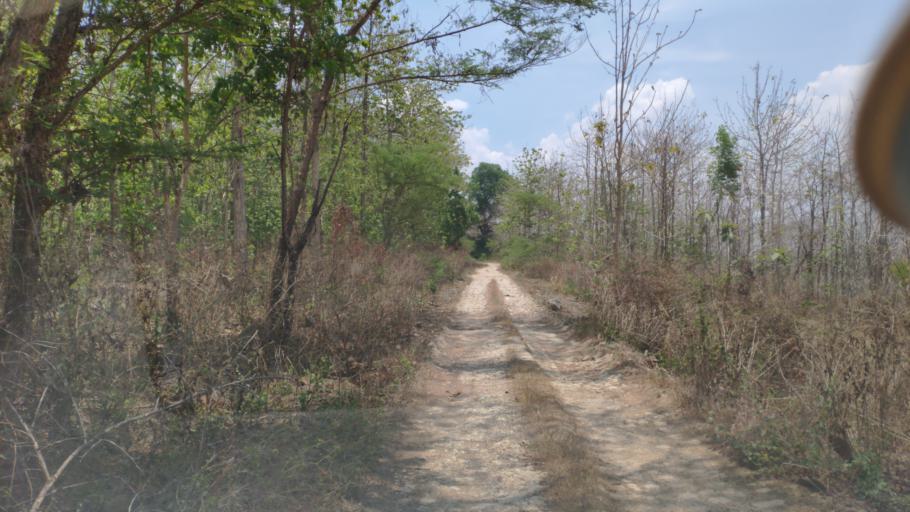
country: ID
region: Central Java
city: Botoh
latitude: -7.0736
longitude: 111.4789
